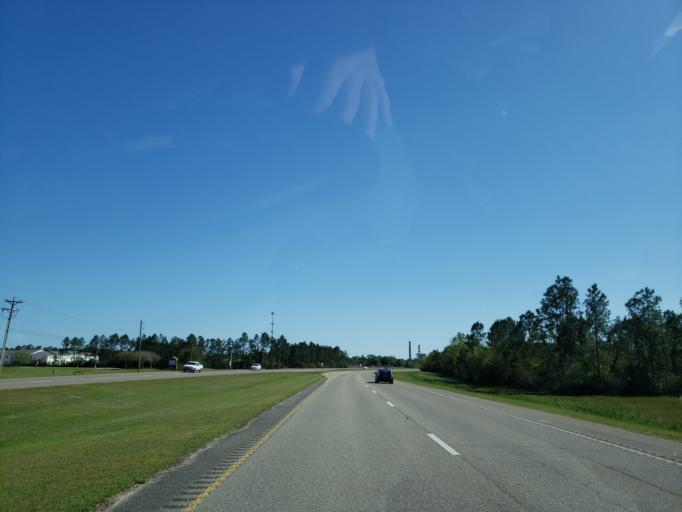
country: US
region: Mississippi
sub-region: Harrison County
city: West Gulfport
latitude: 30.4634
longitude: -89.0270
